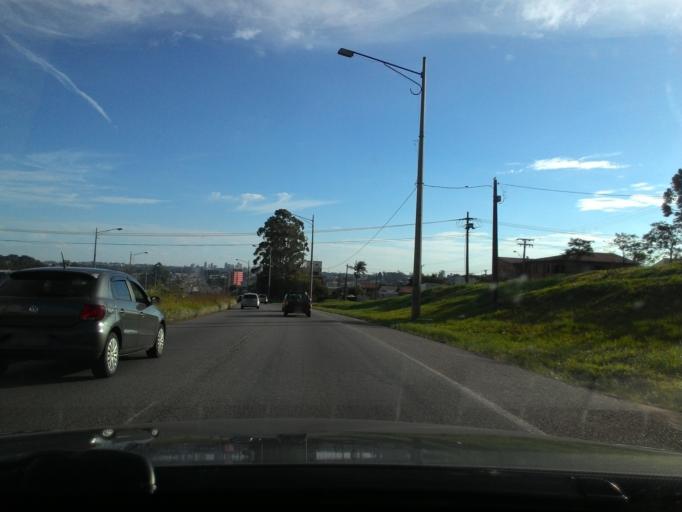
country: BR
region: Parana
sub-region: Pinhais
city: Pinhais
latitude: -25.3976
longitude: -49.2147
